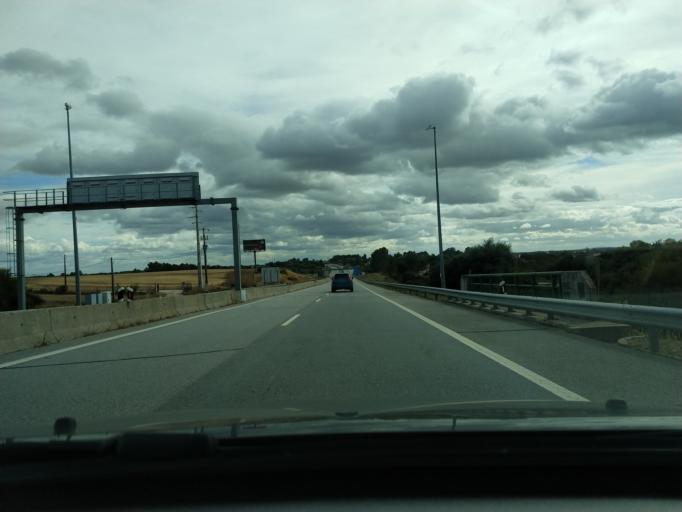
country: PT
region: Castelo Branco
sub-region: Concelho do Fundao
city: Fundao
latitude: 40.0373
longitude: -7.4693
